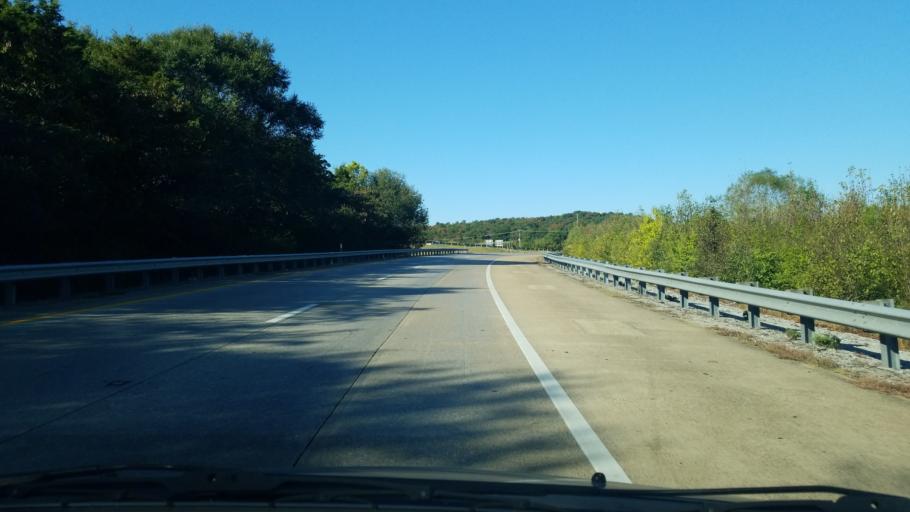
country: US
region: Tennessee
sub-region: Hamilton County
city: East Brainerd
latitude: 35.0289
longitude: -85.1730
